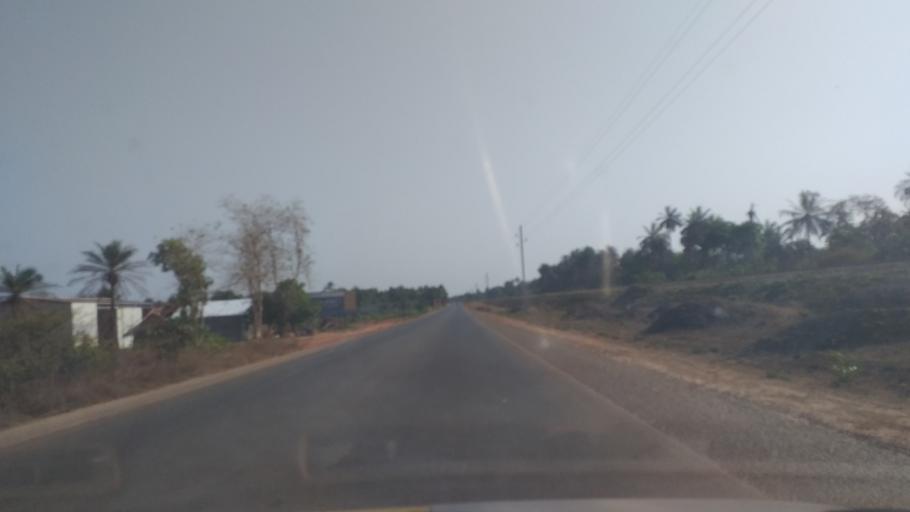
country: GN
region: Boke
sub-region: Boke Prefecture
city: Kamsar
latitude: 10.7475
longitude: -14.5095
